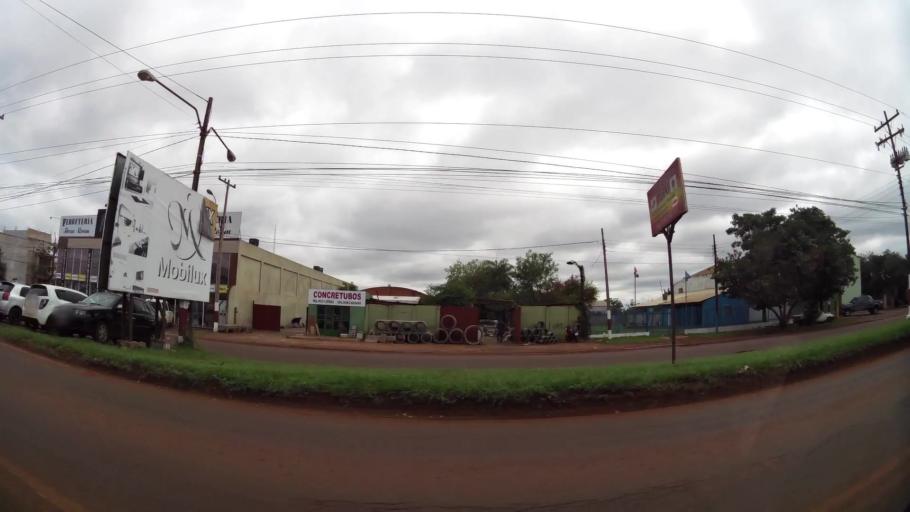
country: PY
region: Alto Parana
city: Ciudad del Este
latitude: -25.3904
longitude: -54.6392
